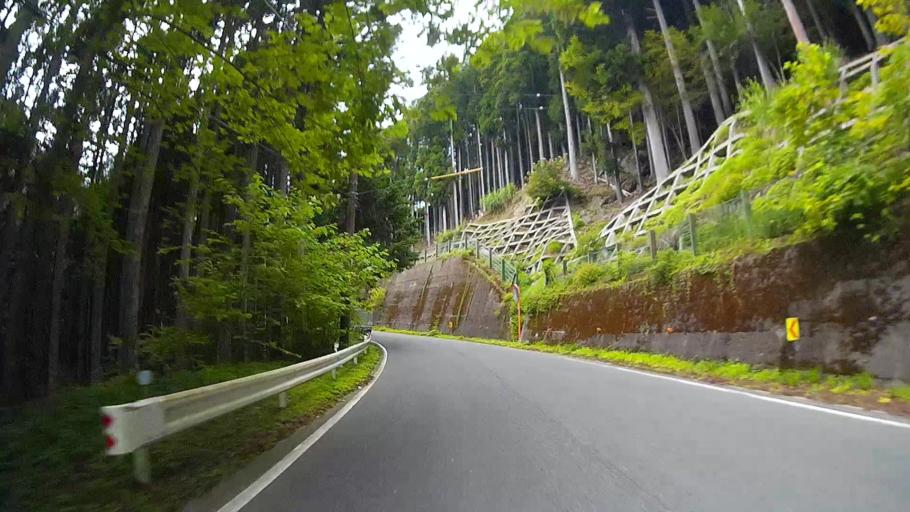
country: JP
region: Saitama
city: Chichibu
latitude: 35.9348
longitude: 138.8424
